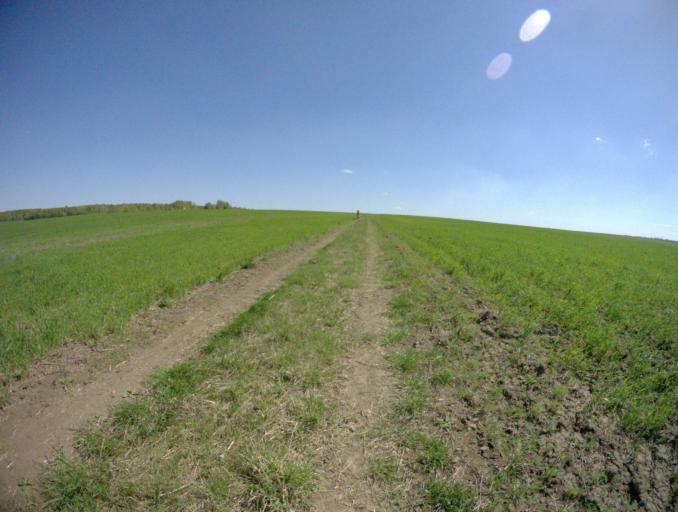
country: RU
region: Vladimir
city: Suzdal'
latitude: 56.2914
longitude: 40.3882
